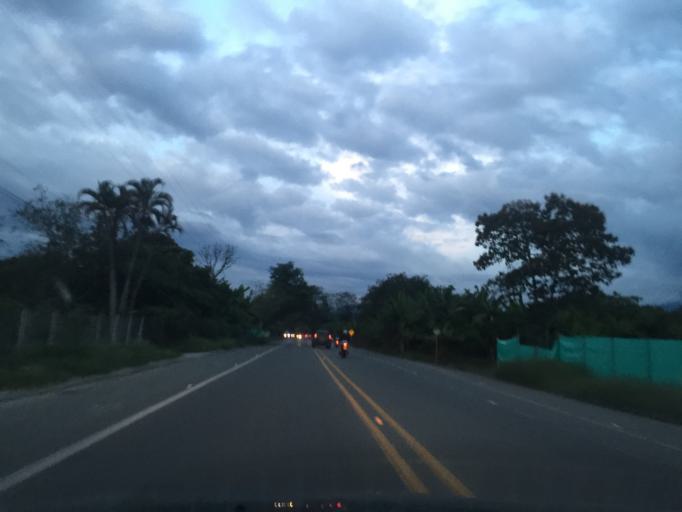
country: CO
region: Quindio
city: La Tebaida
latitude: 4.4911
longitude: -75.7396
